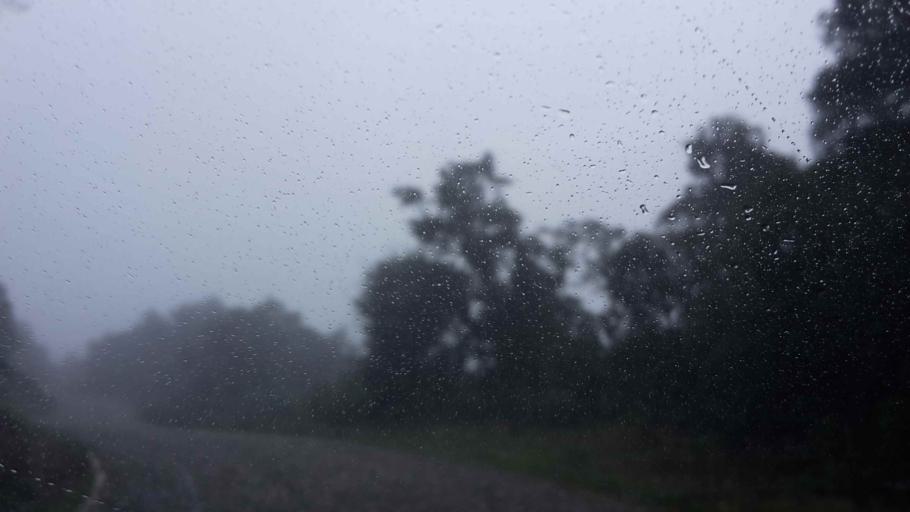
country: BO
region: Cochabamba
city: Colomi
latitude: -17.1662
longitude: -65.8952
